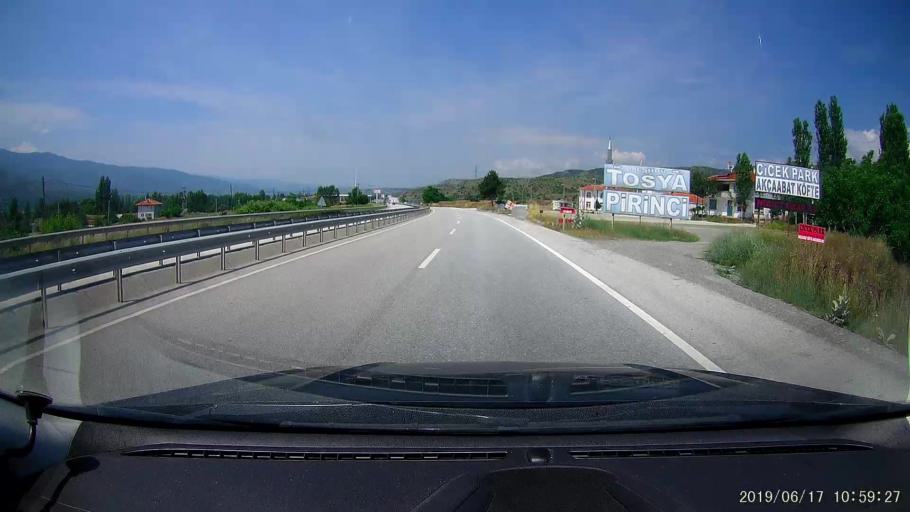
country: TR
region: Kastamonu
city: Tosya
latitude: 41.0409
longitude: 34.2025
